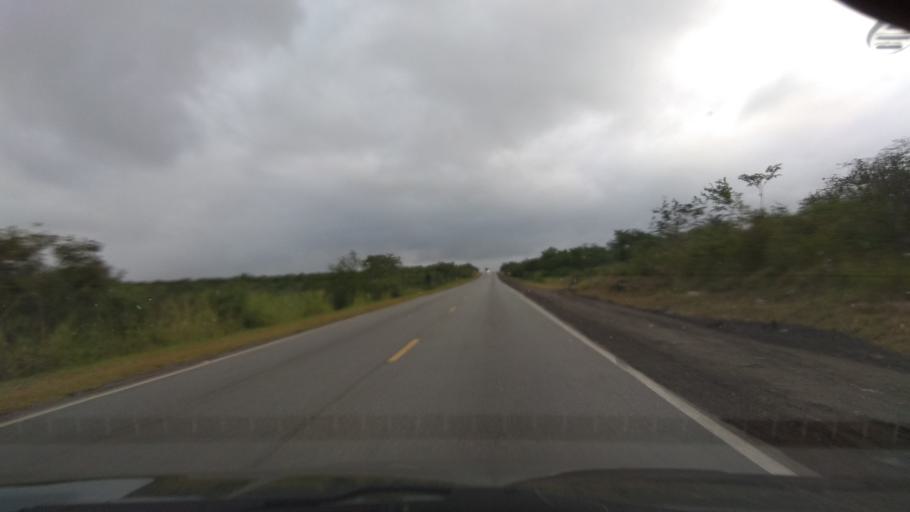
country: BR
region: Bahia
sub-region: Jaguaquara
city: Jaguaquara
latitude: -13.4170
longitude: -40.0263
